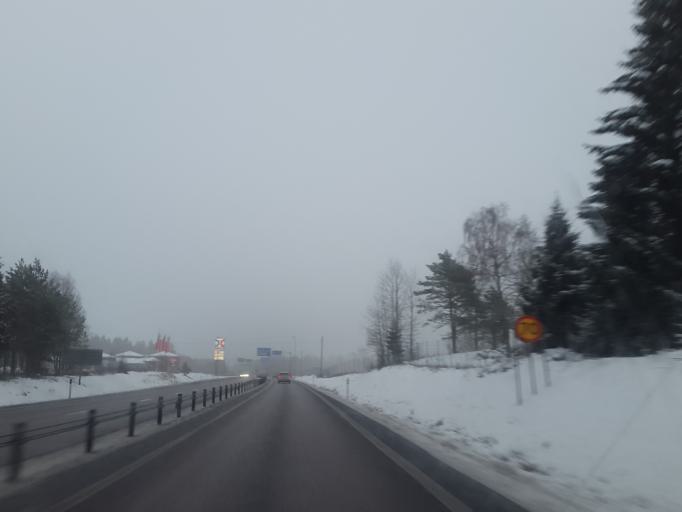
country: SE
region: Vaestra Goetaland
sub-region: Ulricehamns Kommun
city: Ulricehamn
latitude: 57.7802
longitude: 13.6581
